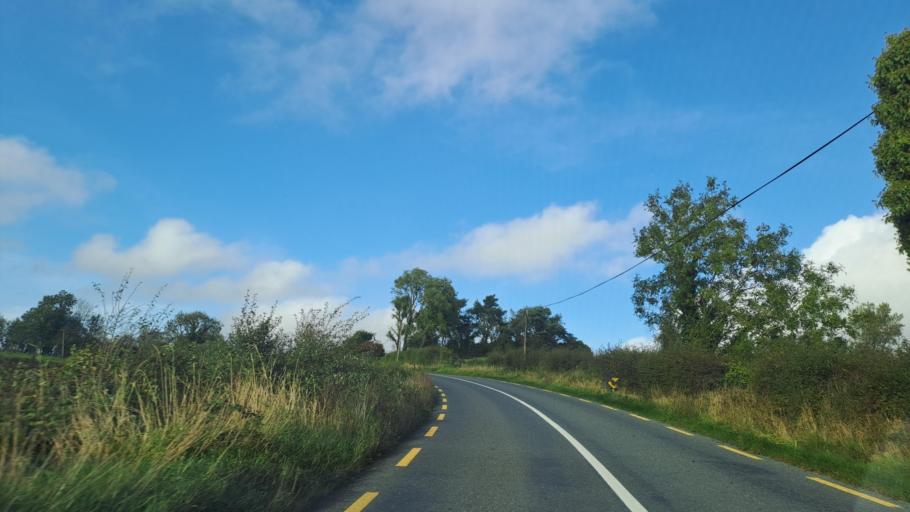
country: IE
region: Ulster
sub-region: An Cabhan
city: Cootehill
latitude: 54.0557
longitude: -7.0149
